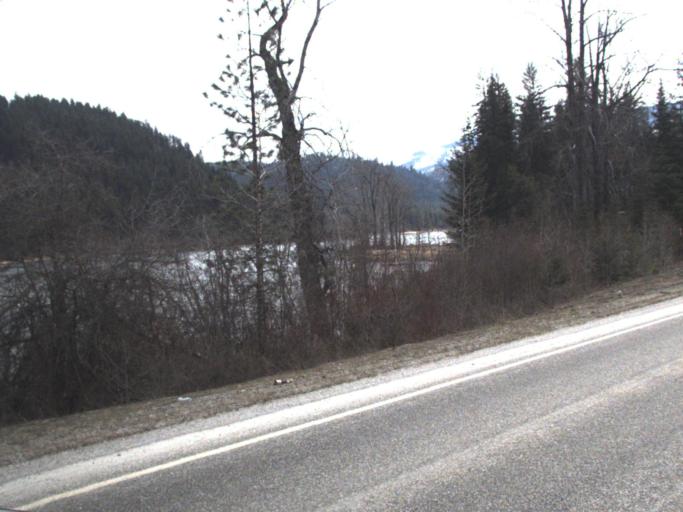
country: US
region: Washington
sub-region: Pend Oreille County
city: Newport
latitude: 48.5244
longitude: -117.3021
